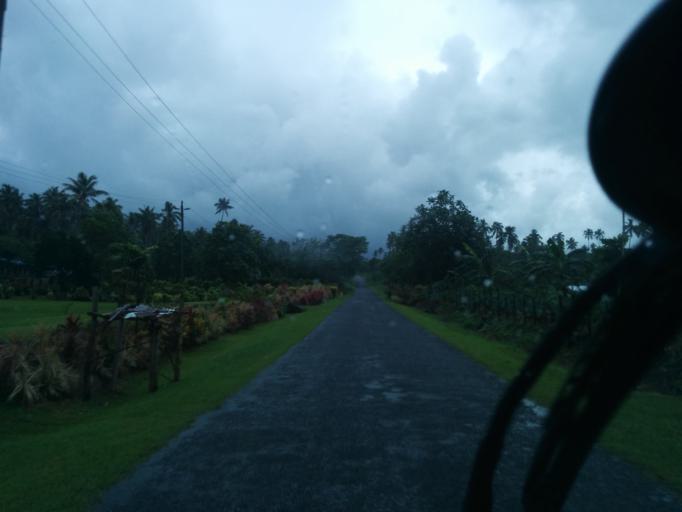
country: WS
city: Matavai
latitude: -14.0281
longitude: -171.6144
